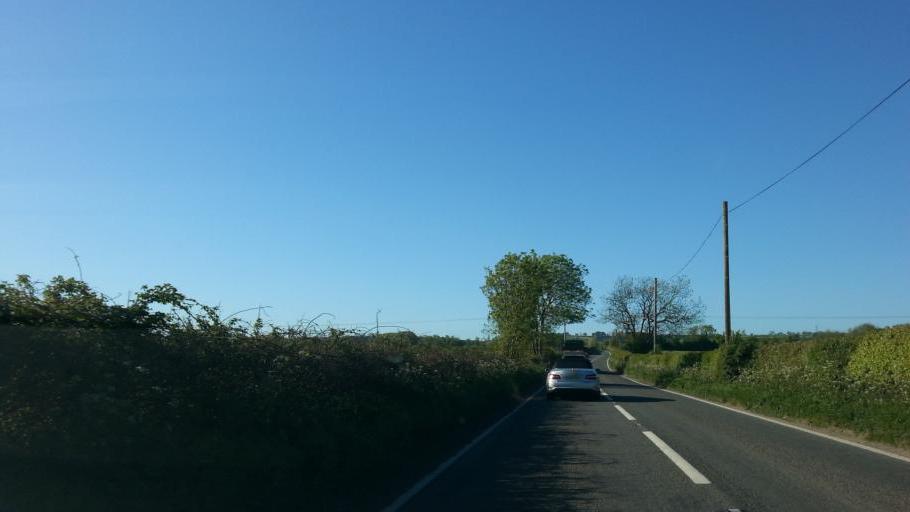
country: GB
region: England
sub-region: Somerset
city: Evercreech
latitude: 51.1458
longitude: -2.5214
